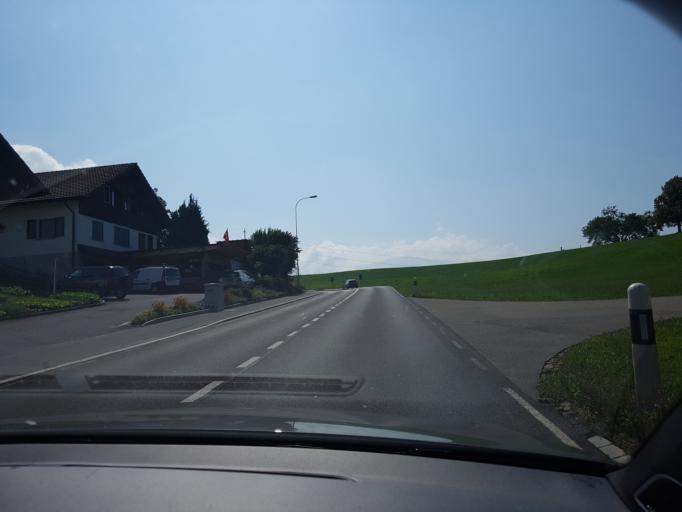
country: CH
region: Saint Gallen
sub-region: Wahlkreis See-Gaster
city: Gommiswald
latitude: 47.2509
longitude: 9.0092
